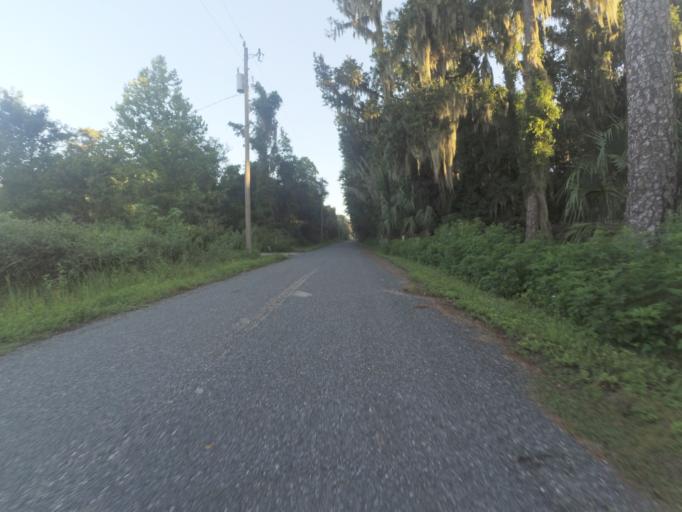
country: US
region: Florida
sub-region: Lake County
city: Astor
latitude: 29.2837
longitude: -81.6478
